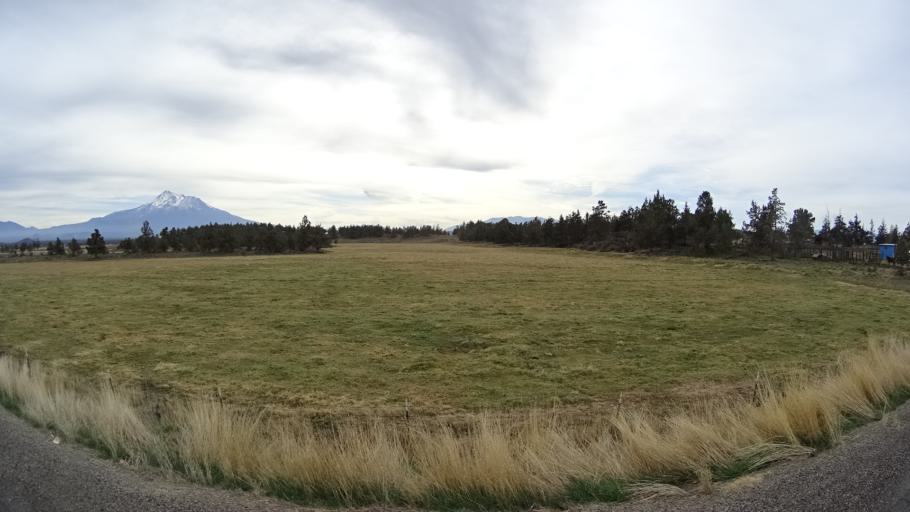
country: US
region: California
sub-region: Siskiyou County
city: Montague
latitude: 41.6241
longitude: -122.4174
